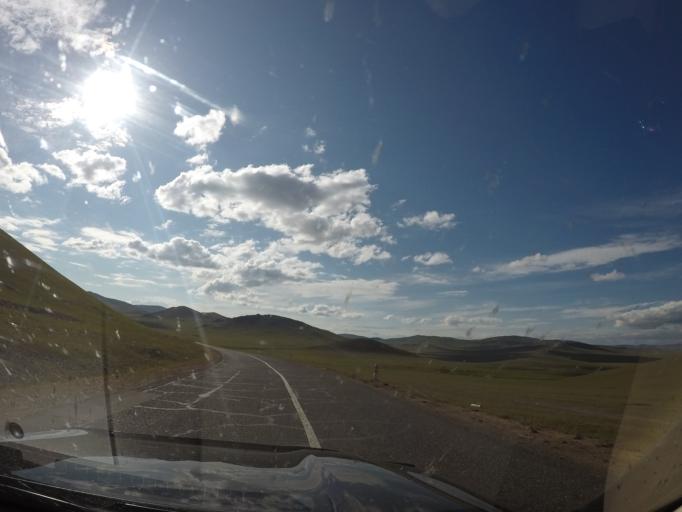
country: MN
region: Hentiy
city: Modot
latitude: 47.7523
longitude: 108.9545
